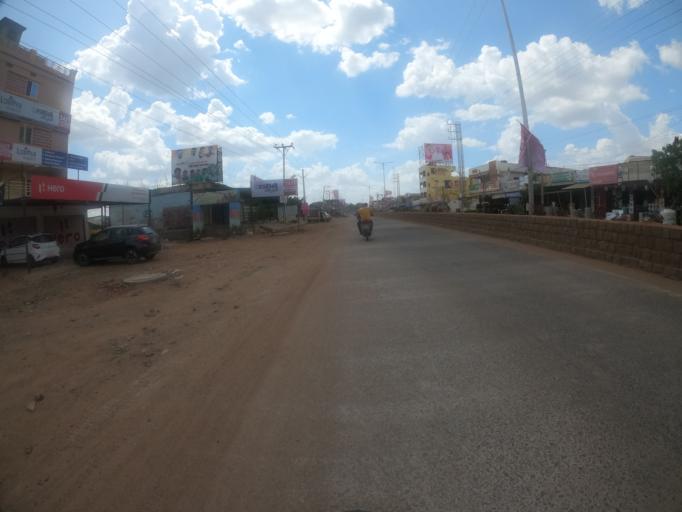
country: IN
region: Telangana
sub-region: Rangareddi
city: Sriramnagar
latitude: 17.3105
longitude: 78.1414
